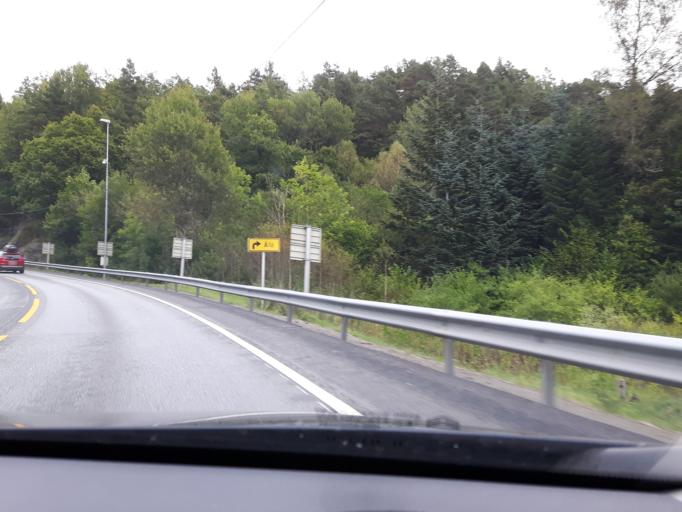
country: NO
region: Vest-Agder
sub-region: Marnardal
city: Helland
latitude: 58.0791
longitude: 7.6135
